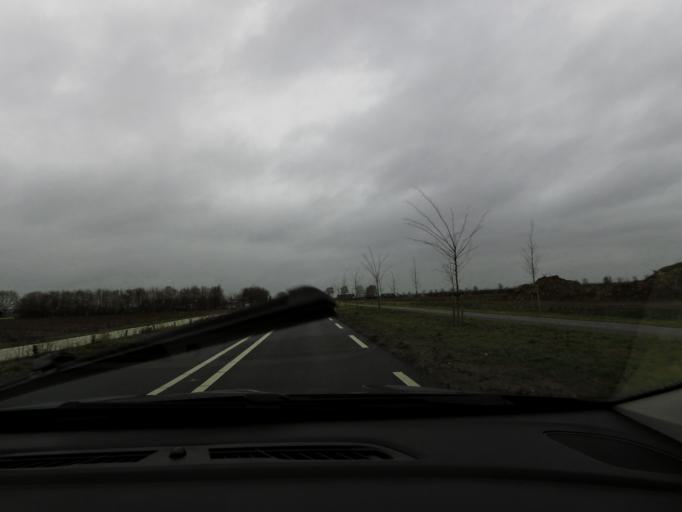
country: NL
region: North Brabant
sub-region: Gemeente Waalwijk
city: Waspik
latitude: 51.7316
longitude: 4.9253
